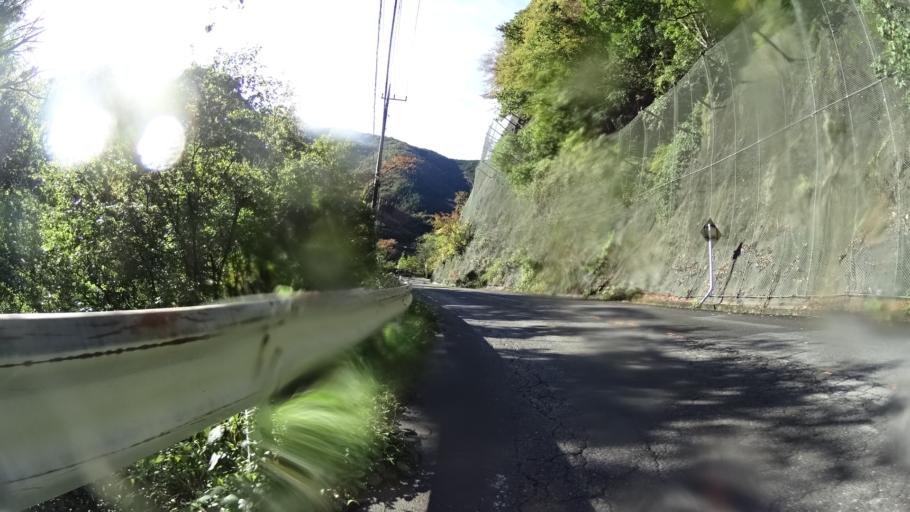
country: JP
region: Yamanashi
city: Otsuki
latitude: 35.7889
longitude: 138.9359
